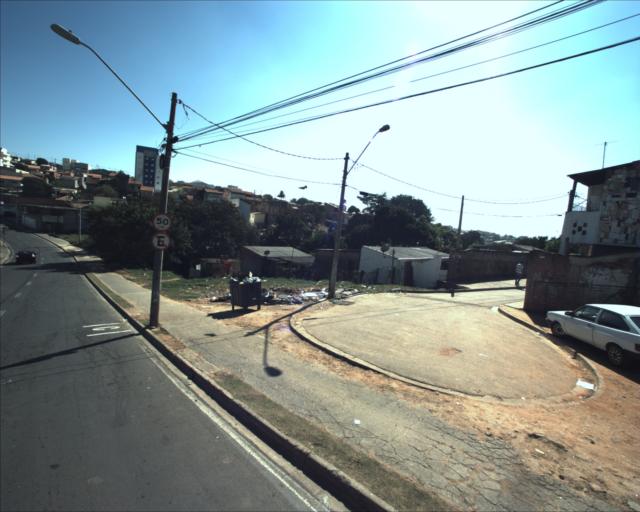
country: BR
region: Sao Paulo
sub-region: Sorocaba
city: Sorocaba
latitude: -23.5052
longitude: -47.5062
